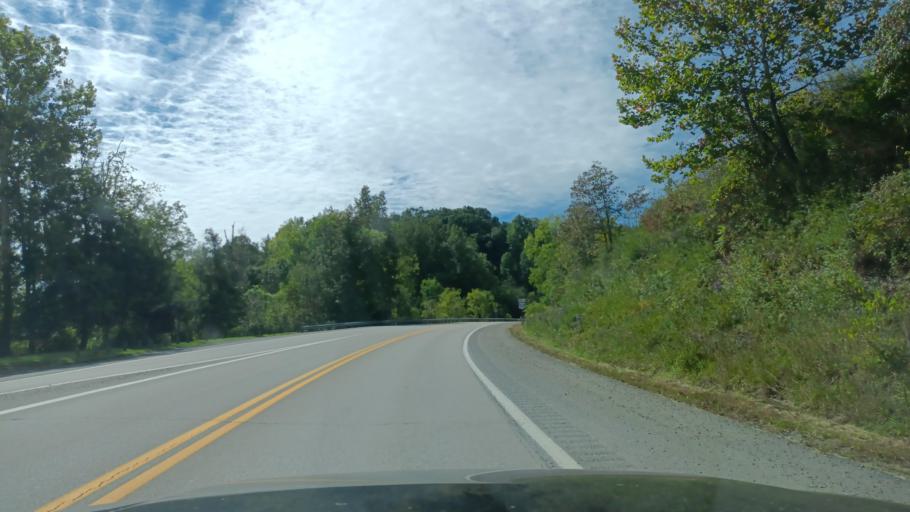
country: US
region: West Virginia
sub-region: Harrison County
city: Bridgeport
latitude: 39.2876
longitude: -80.2290
